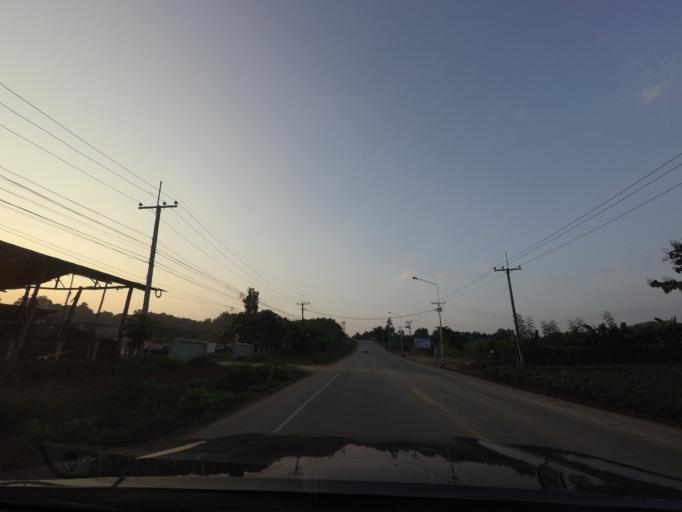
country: TH
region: Nan
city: Na Noi
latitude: 18.3630
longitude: 100.7094
